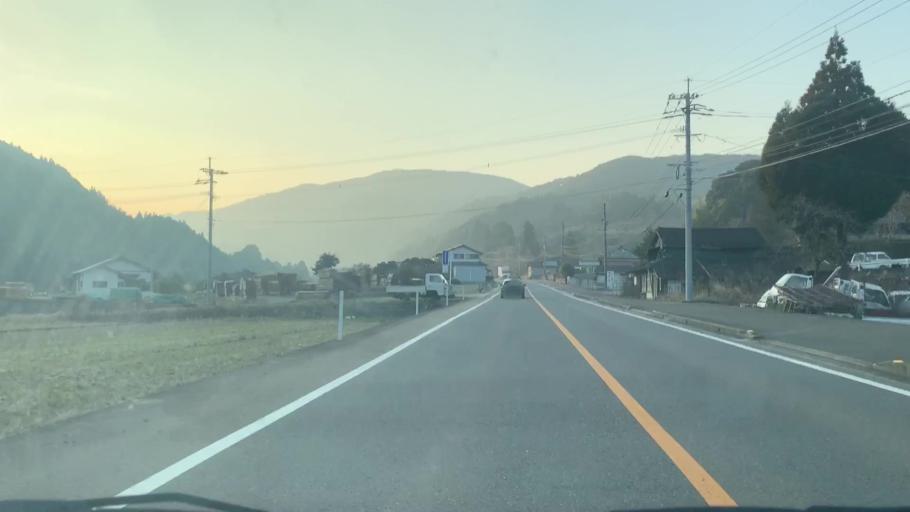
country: JP
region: Saga Prefecture
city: Takeocho-takeo
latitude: 33.2638
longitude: 130.0440
